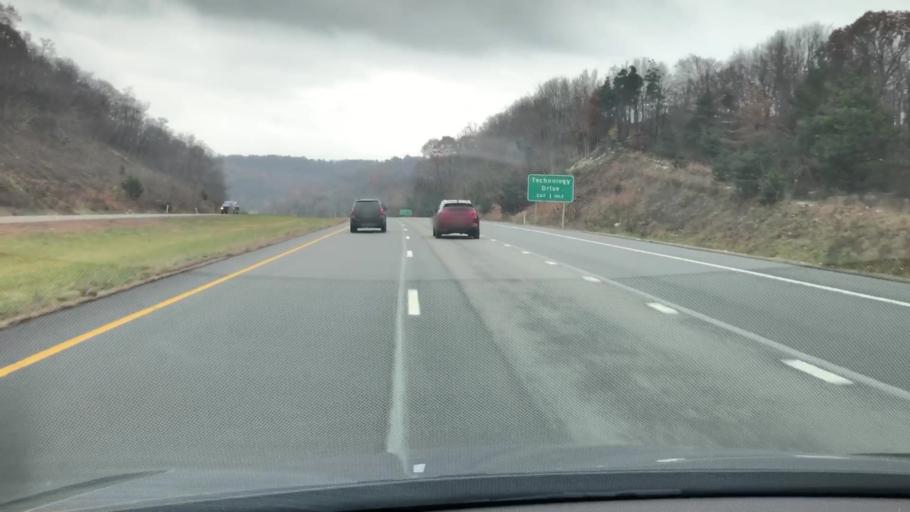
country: US
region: Pennsylvania
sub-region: Westmoreland County
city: New Stanton
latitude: 40.2172
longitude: -79.5919
